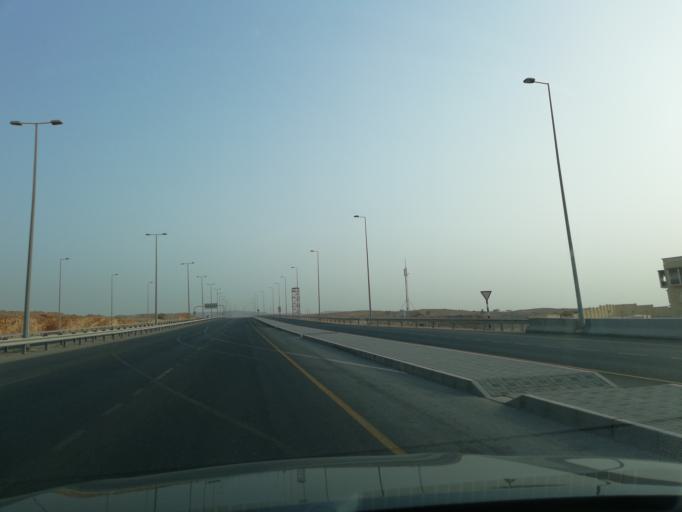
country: OM
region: Muhafazat Masqat
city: Bawshar
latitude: 23.5705
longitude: 58.2949
